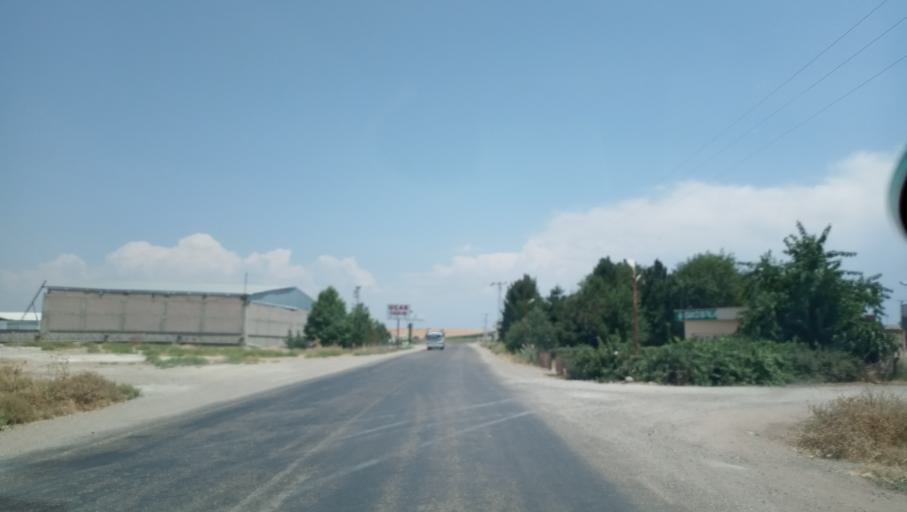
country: TR
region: Diyarbakir
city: Aralik
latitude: 37.8266
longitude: 40.6831
